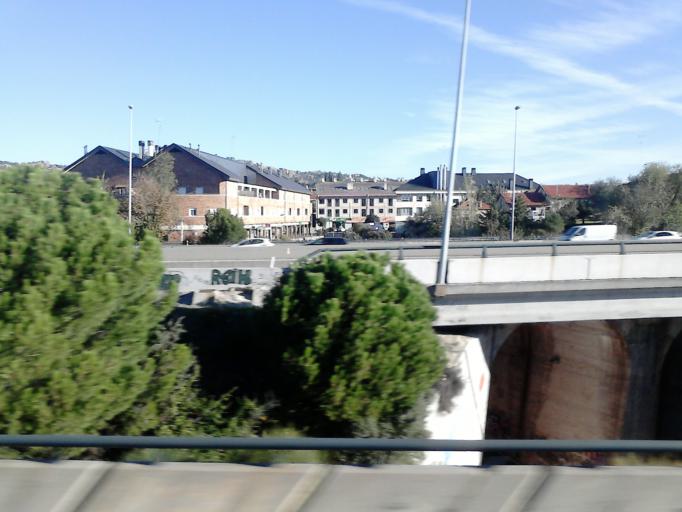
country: ES
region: Madrid
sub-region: Provincia de Madrid
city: Torrelodones
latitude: 40.5743
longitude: -3.9313
